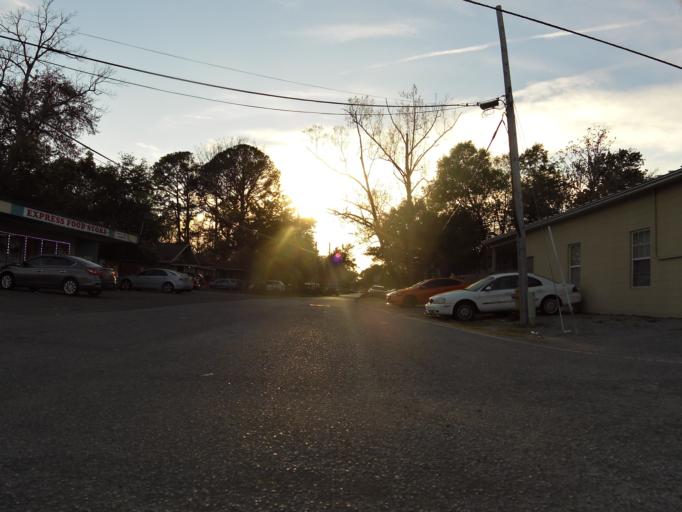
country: US
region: Florida
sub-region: Duval County
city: Jacksonville
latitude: 30.2883
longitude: -81.6440
